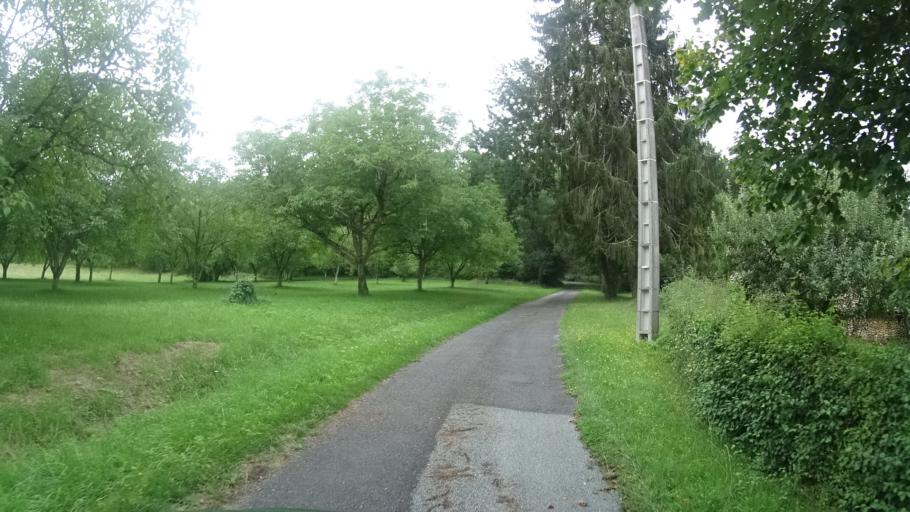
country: FR
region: Aquitaine
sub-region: Departement de la Dordogne
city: Lembras
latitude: 44.9883
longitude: 0.5221
